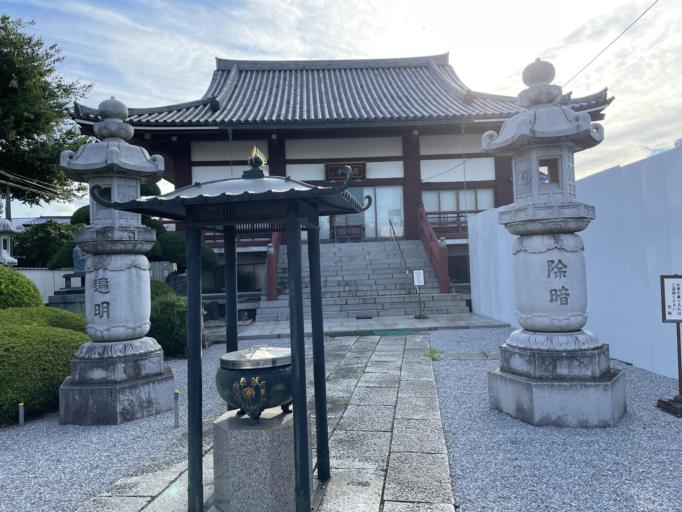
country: JP
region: Saitama
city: Yashio-shi
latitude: 35.7689
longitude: 139.8388
